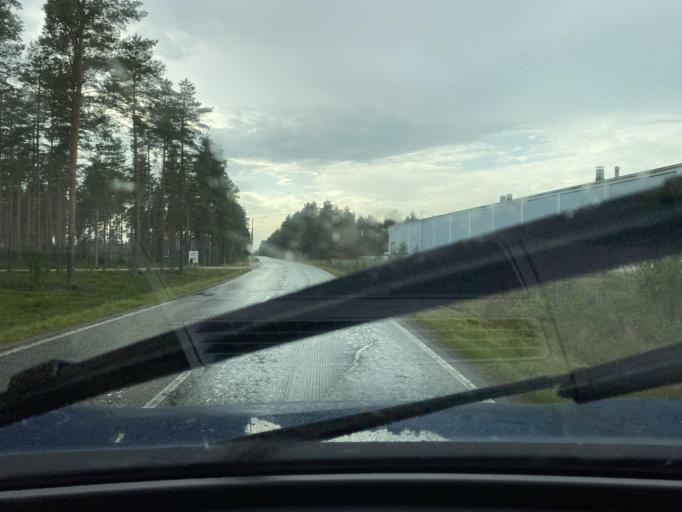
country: FI
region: Central Ostrobothnia
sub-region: Kaustinen
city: Veteli
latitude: 63.4684
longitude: 23.8263
